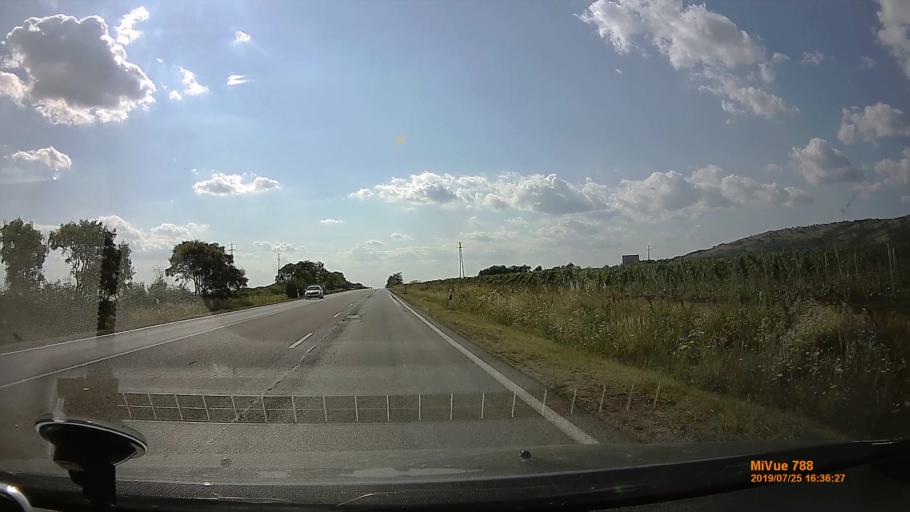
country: HU
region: Heves
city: Abasar
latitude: 47.7693
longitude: 19.9817
